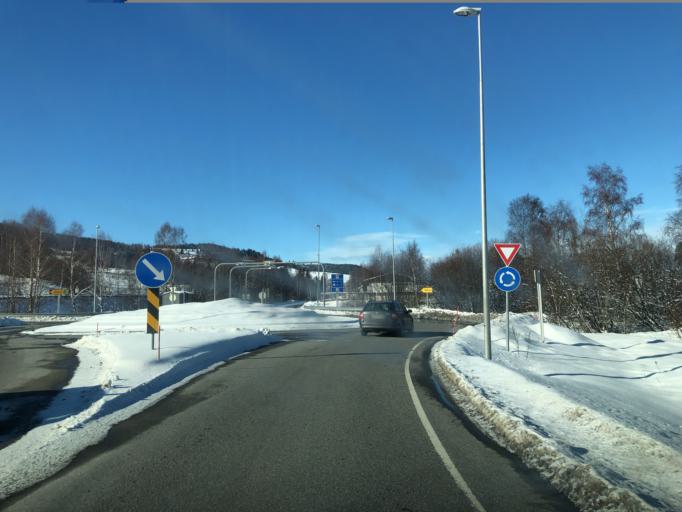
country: NO
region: Oppland
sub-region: Lunner
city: Roa
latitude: 60.3222
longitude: 10.5830
